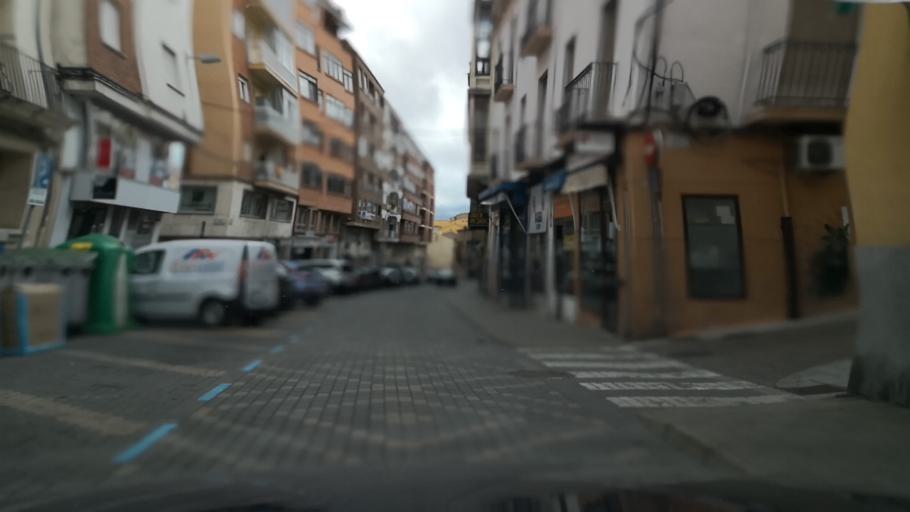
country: ES
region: Castille and Leon
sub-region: Provincia de Zamora
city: Zamora
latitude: 41.5051
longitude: -5.7460
